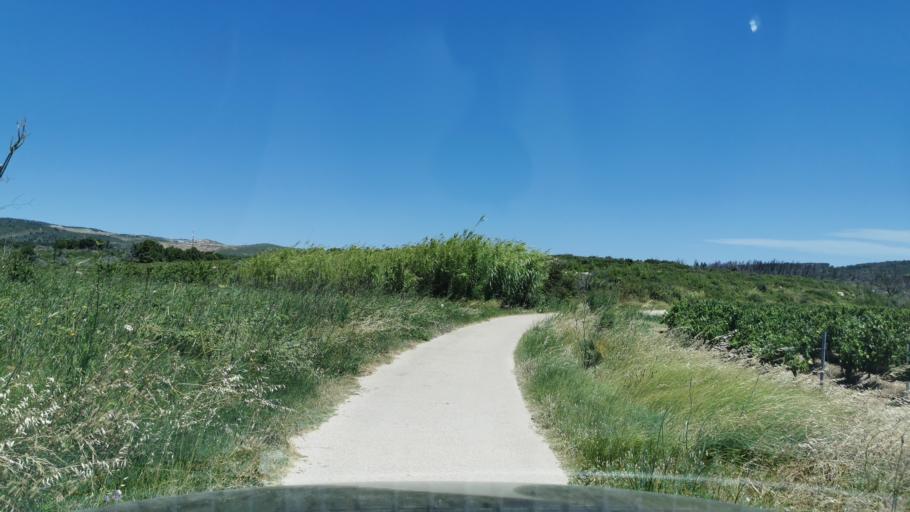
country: FR
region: Languedoc-Roussillon
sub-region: Departement de l'Aude
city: Peyriac-de-Mer
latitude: 43.1046
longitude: 2.9590
